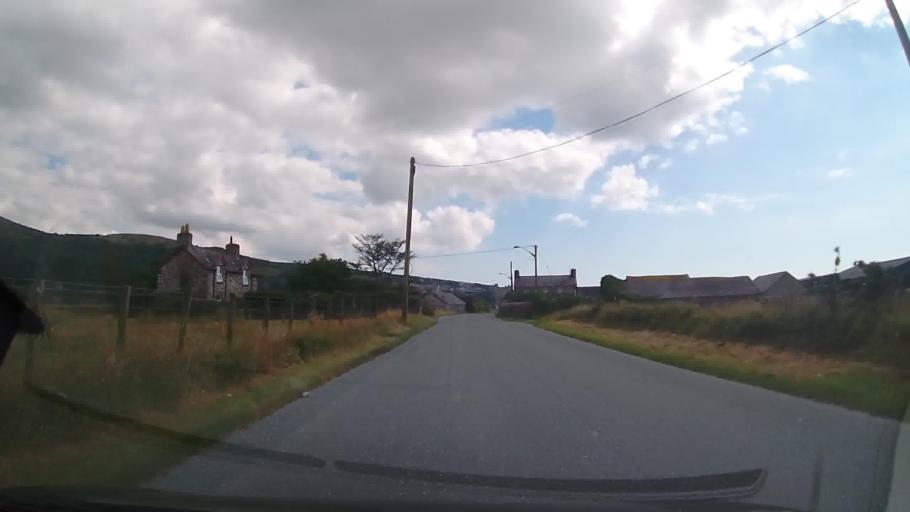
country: GB
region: Wales
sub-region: Gwynedd
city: Llanfair
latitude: 52.8740
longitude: -4.1052
